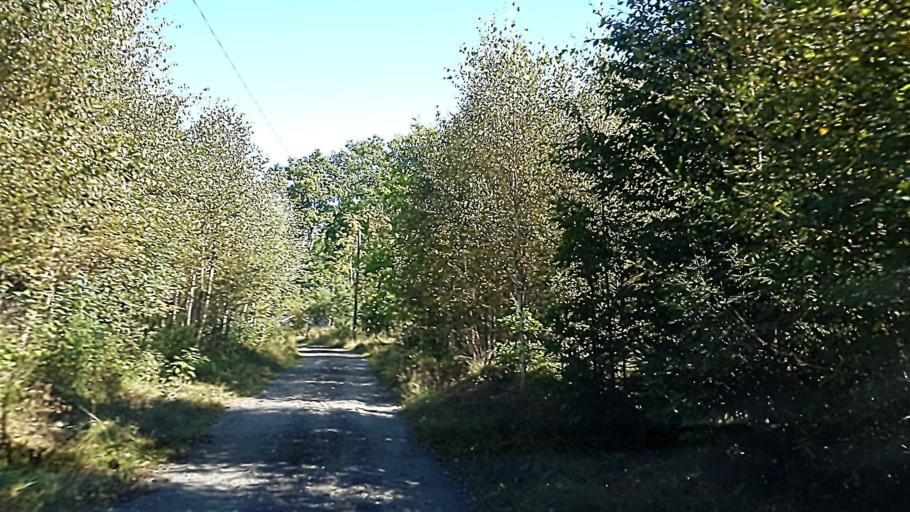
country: SE
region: Kronoberg
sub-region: Ljungby Kommun
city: Ljungby
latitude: 56.8093
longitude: 14.0028
